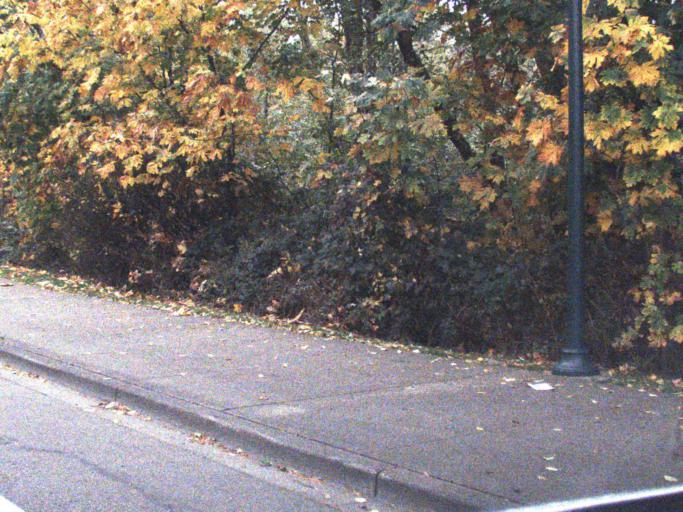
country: US
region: Washington
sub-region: Snohomish County
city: Mukilteo
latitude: 47.9146
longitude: -122.2968
